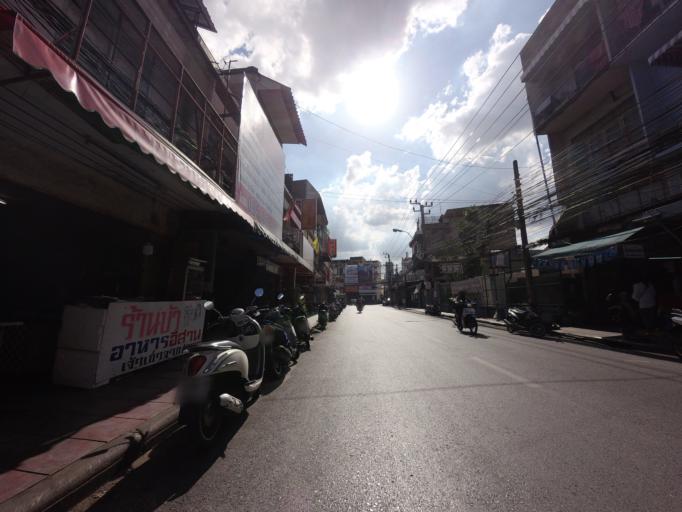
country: TH
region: Bangkok
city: Huai Khwang
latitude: 13.7777
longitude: 100.5810
